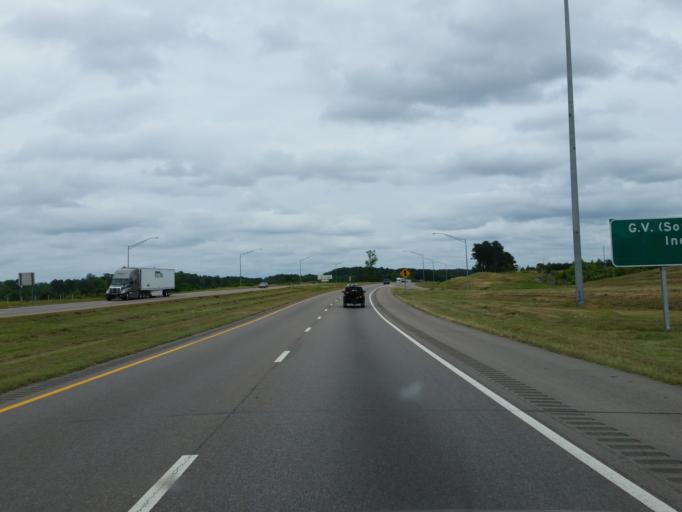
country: US
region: Mississippi
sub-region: Lauderdale County
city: Marion
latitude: 32.3794
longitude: -88.6526
